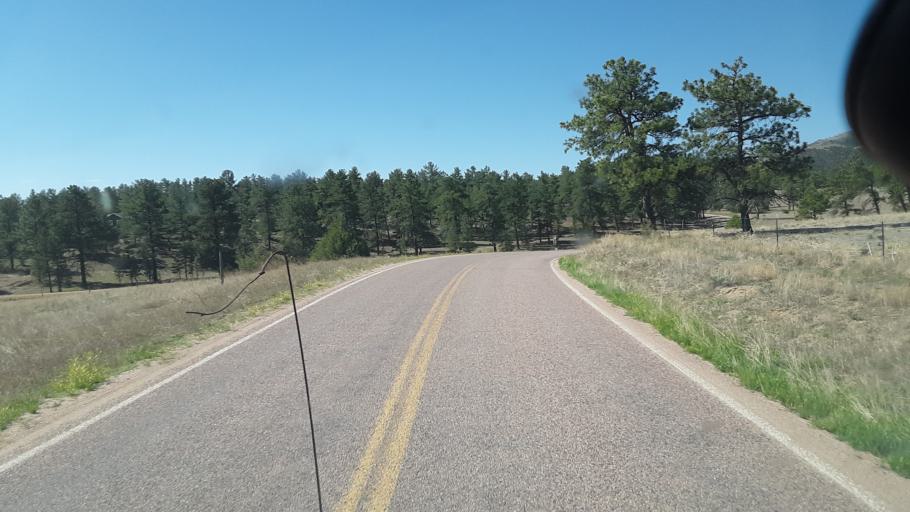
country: US
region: Colorado
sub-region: Custer County
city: Westcliffe
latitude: 38.3540
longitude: -105.4811
